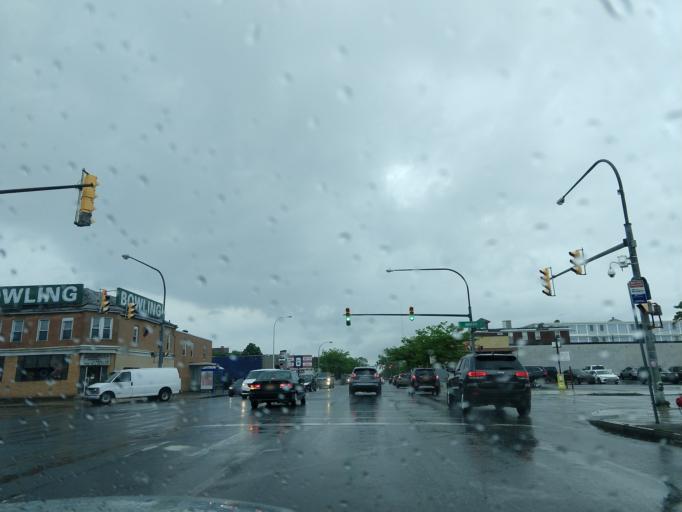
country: US
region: New York
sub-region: Erie County
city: Kenmore
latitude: 42.9403
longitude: -78.8786
